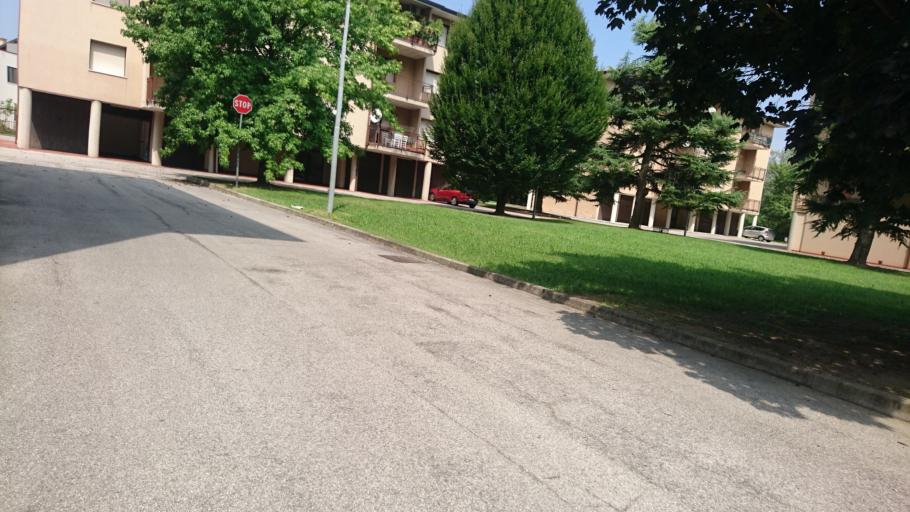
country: IT
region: Veneto
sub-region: Provincia di Padova
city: Padova
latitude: 45.3802
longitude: 11.8872
